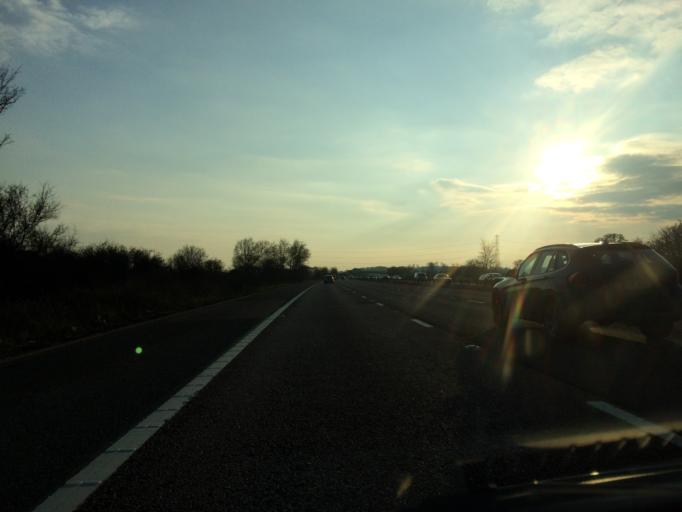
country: GB
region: England
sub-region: Wiltshire
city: Bremhill
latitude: 51.5196
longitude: -2.0522
